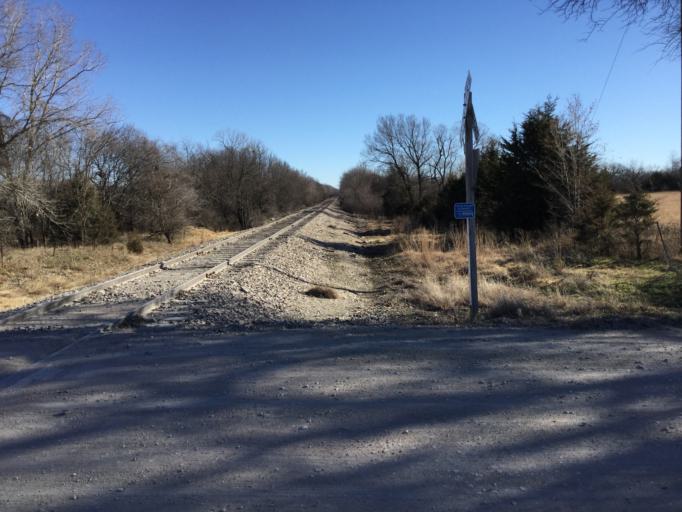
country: US
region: Kansas
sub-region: Butler County
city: Towanda
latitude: 37.7940
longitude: -97.0806
